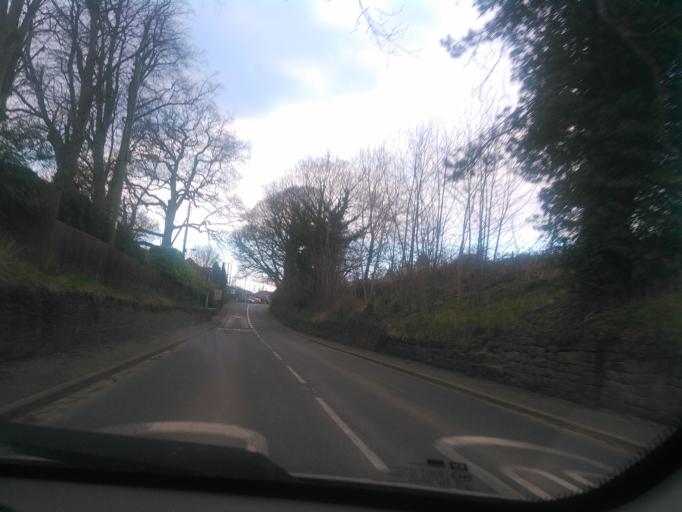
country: GB
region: England
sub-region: Telford and Wrekin
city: Chetwynd
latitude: 52.8354
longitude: -2.4559
